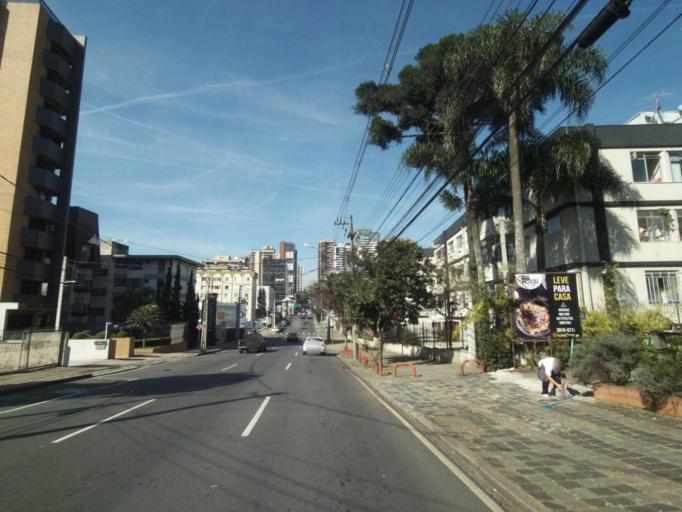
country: BR
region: Parana
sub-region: Curitiba
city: Curitiba
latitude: -25.4411
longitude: -49.2900
